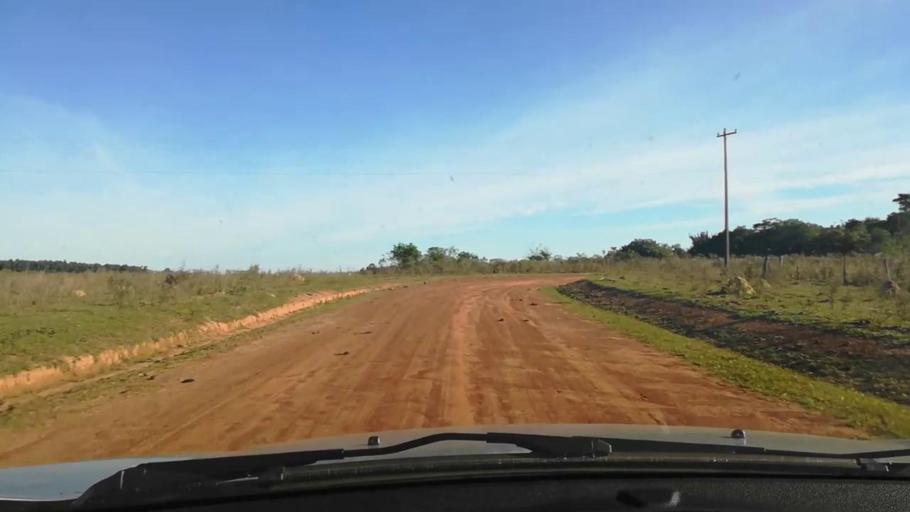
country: PY
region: Caaguazu
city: Coronel Oviedo
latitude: -25.5178
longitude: -56.4104
